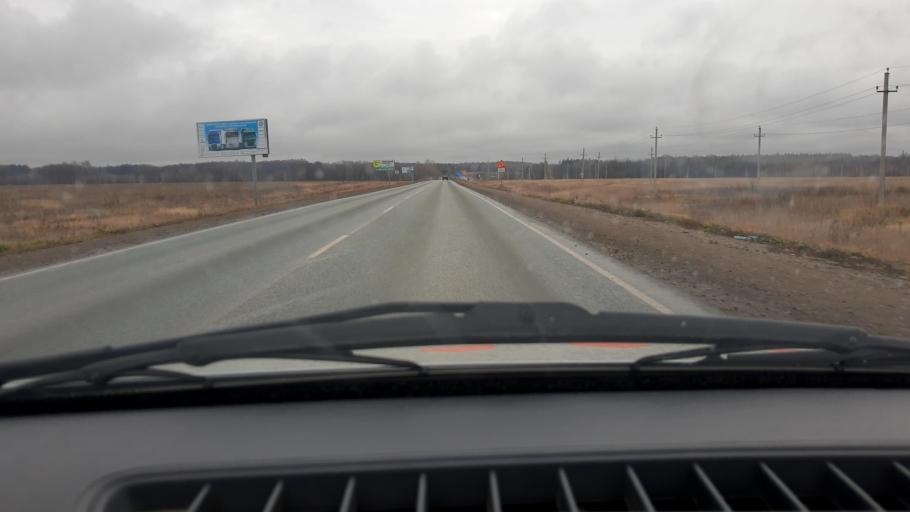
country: RU
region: Bashkortostan
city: Iglino
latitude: 54.7503
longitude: 56.2913
